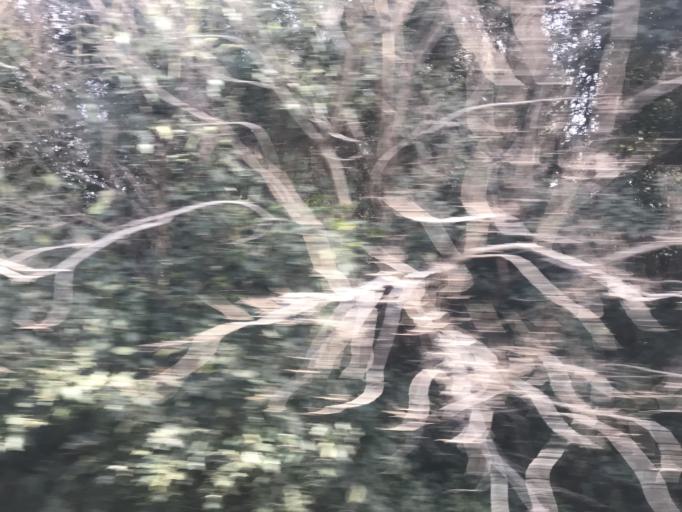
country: AR
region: Cordoba
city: Laguna Larga
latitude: -31.8033
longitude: -63.7799
